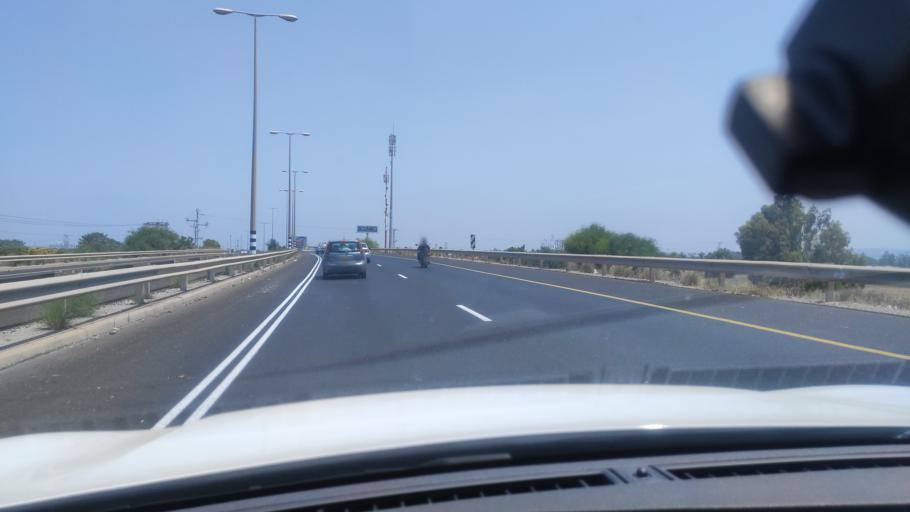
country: IL
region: Central District
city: Petah Tiqwa
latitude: 32.1098
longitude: 34.9021
